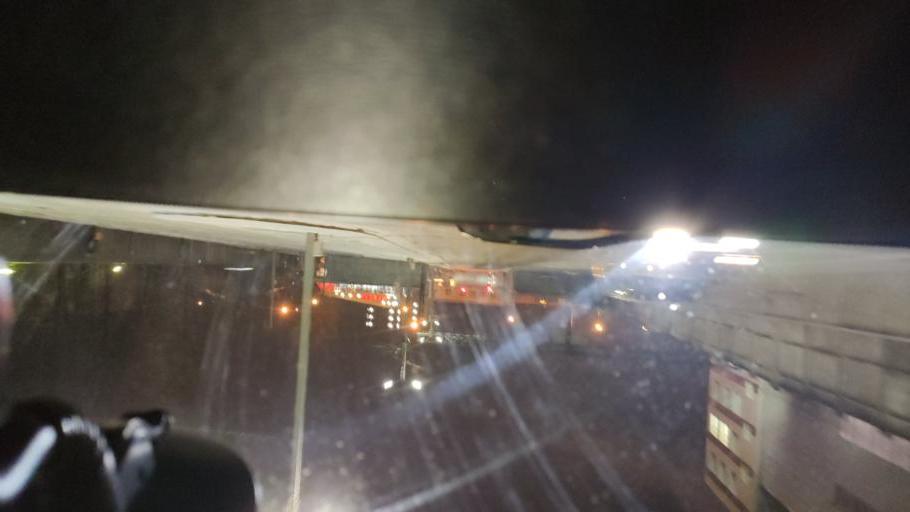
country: RU
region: Perm
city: Perm
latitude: 57.9836
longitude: 56.2611
